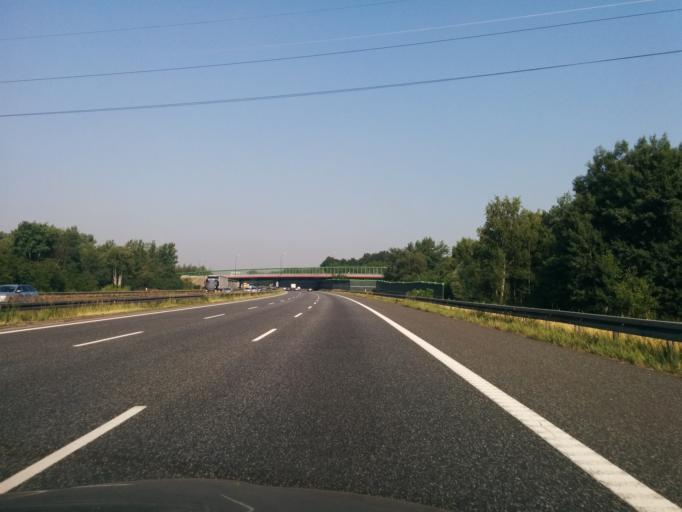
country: PL
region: Silesian Voivodeship
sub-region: Powiat gliwicki
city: Przyszowice
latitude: 50.2675
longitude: 18.7745
